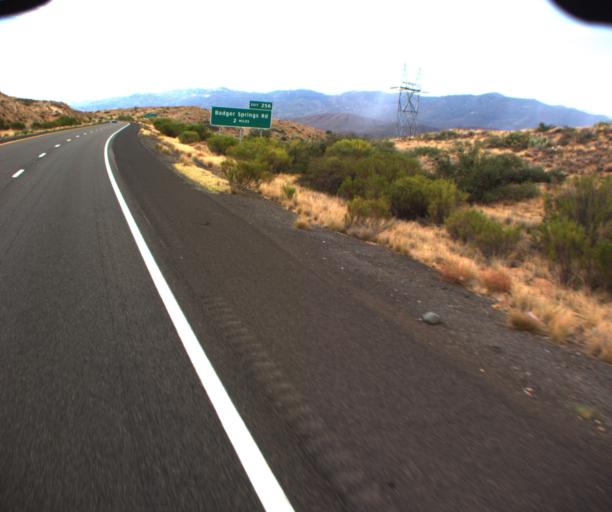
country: US
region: Arizona
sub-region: Yavapai County
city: Cordes Lakes
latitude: 34.2676
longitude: -112.1151
